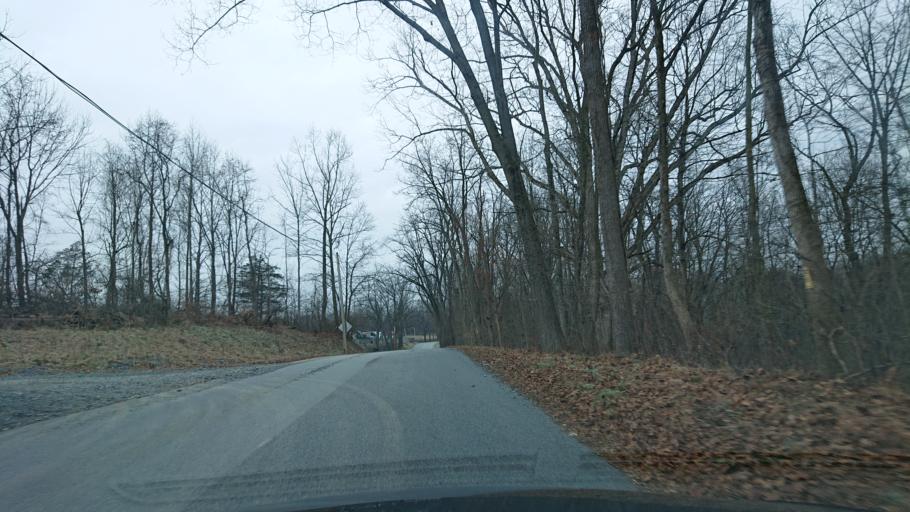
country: US
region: Pennsylvania
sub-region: Lebanon County
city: Palmyra
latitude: 40.3825
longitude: -76.6223
